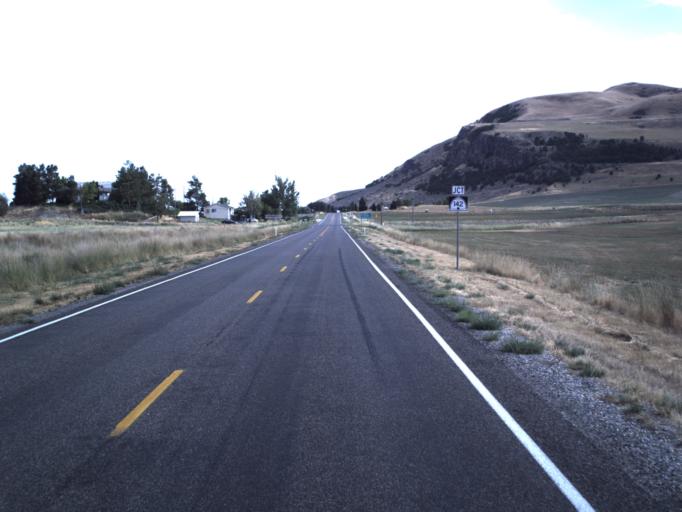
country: US
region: Utah
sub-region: Cache County
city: Lewiston
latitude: 41.9200
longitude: -111.9529
